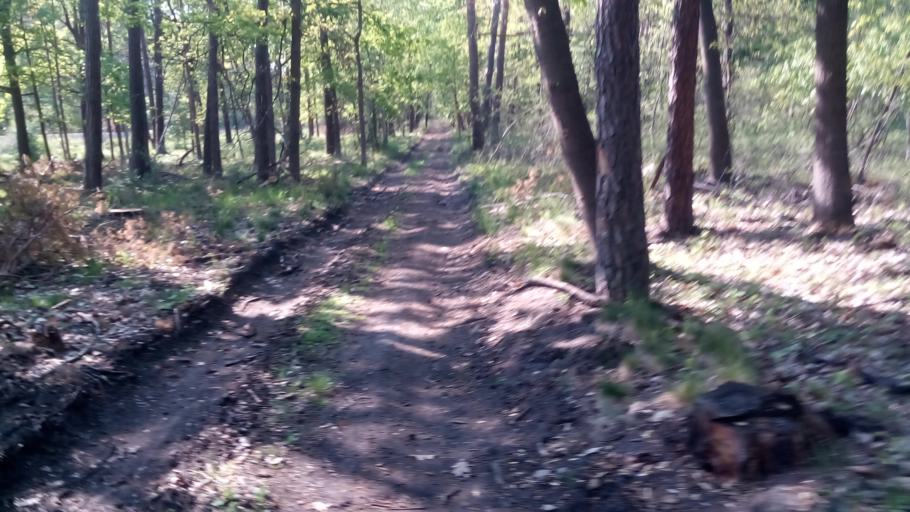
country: PL
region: Opole Voivodeship
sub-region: Powiat opolski
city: Tarnow Opolski
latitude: 50.5855
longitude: 18.0530
